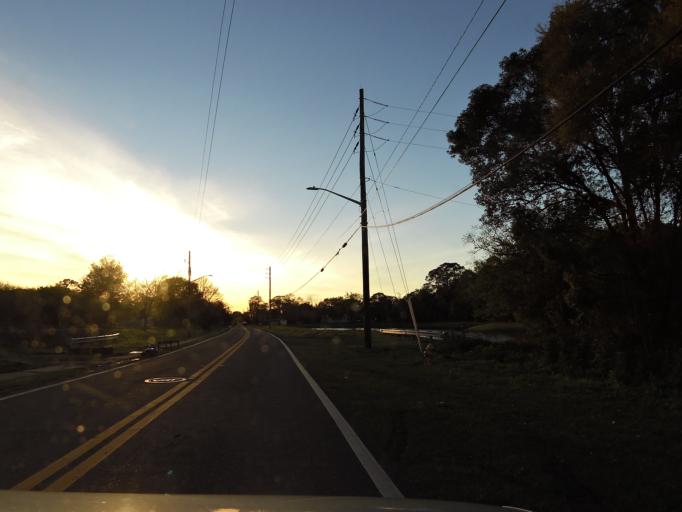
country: US
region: Florida
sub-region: Duval County
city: Jacksonville
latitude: 30.3402
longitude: -81.7265
